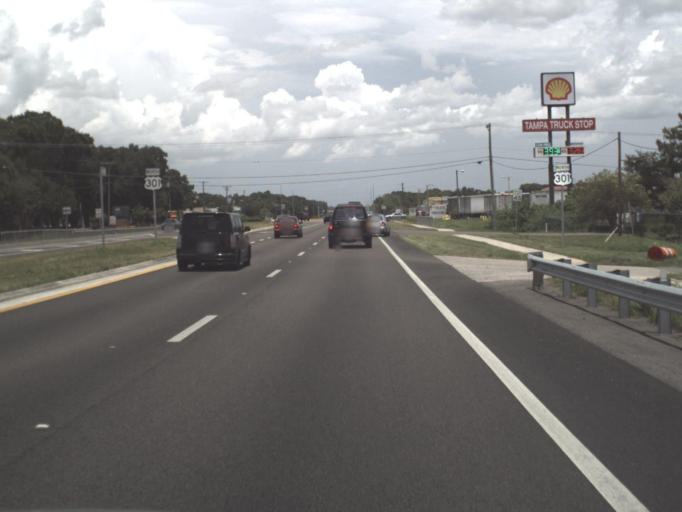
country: US
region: Florida
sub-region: Hillsborough County
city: East Lake-Orient Park
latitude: 28.0025
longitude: -82.3563
